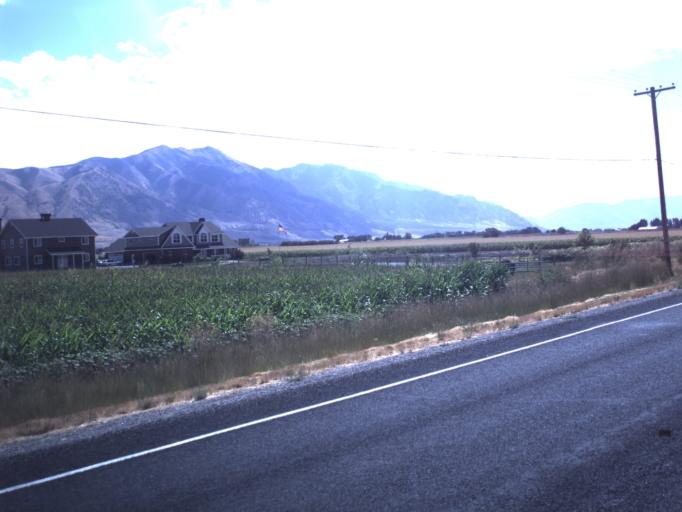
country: US
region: Utah
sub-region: Box Elder County
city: Garland
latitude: 41.7600
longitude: -112.1486
